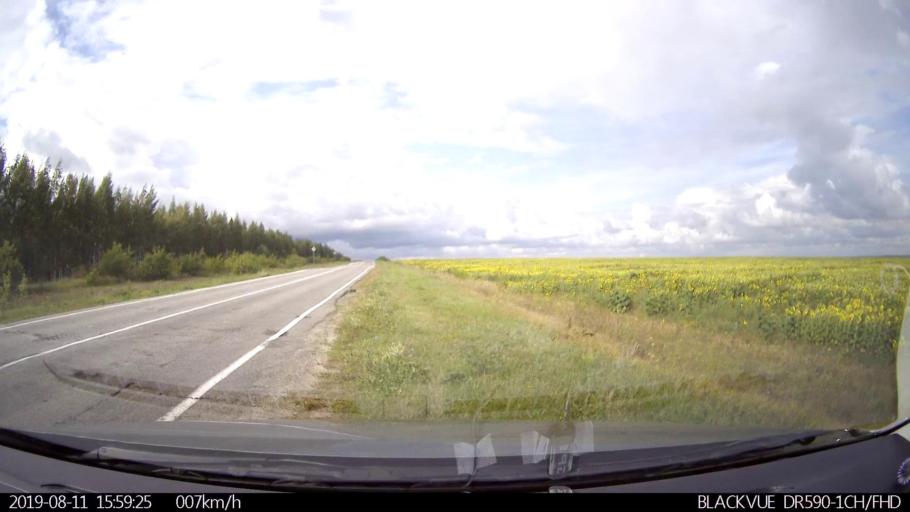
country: RU
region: Ulyanovsk
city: Ignatovka
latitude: 53.9603
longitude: 47.6490
